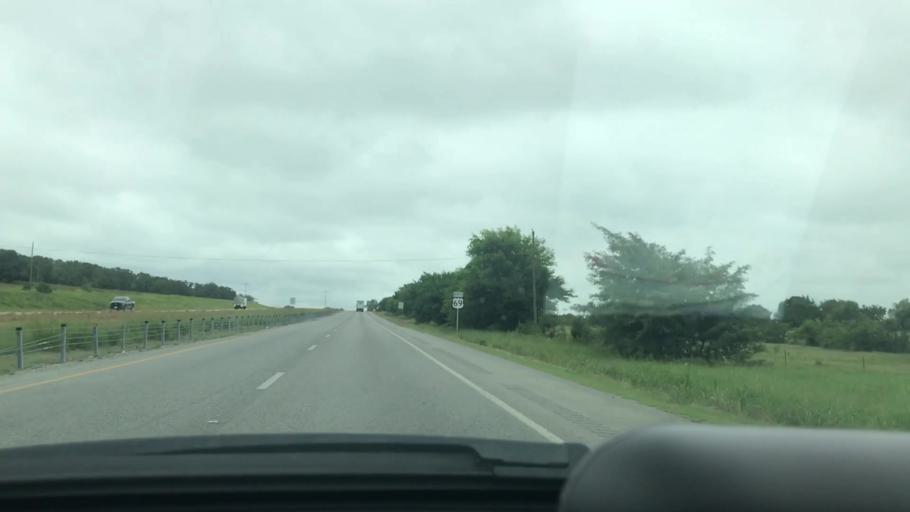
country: US
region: Oklahoma
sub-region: Coal County
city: Coalgate
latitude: 34.6662
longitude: -95.9378
